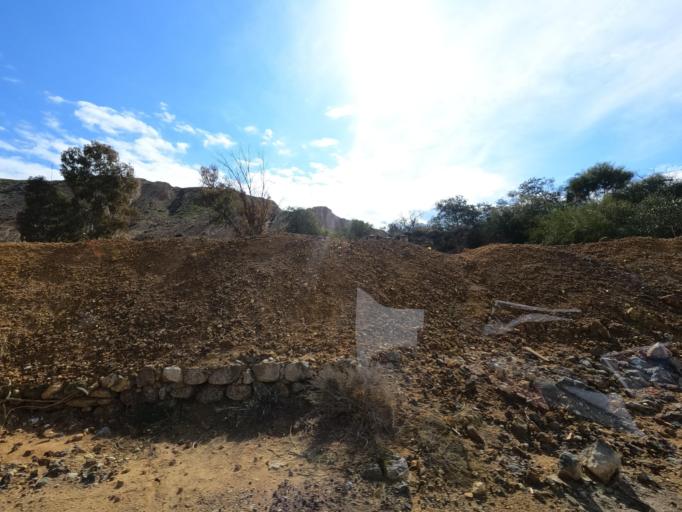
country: CY
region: Lefkosia
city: Lefka
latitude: 35.0981
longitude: 32.8859
